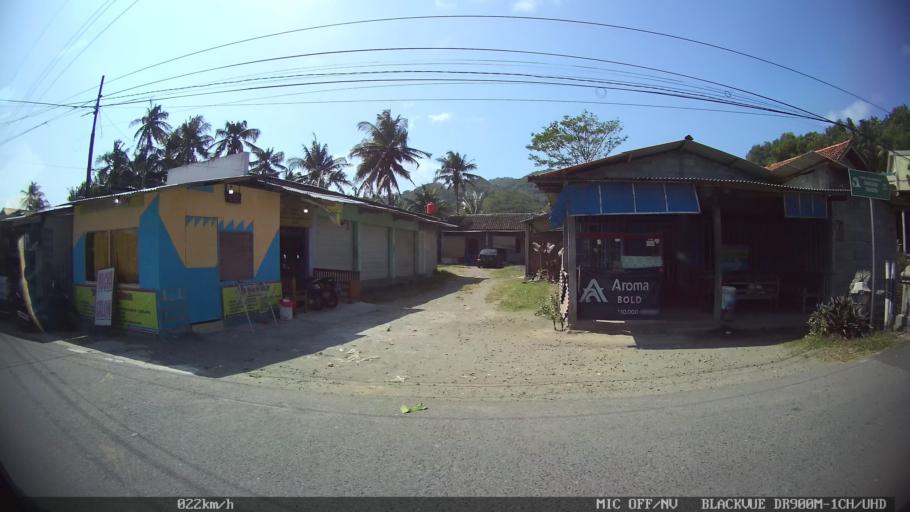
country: ID
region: Daerah Istimewa Yogyakarta
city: Pundong
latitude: -8.0197
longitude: 110.3263
